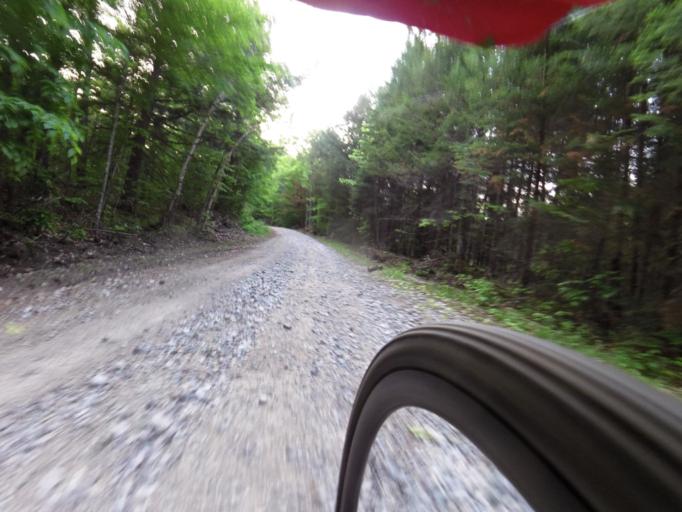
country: CA
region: Ontario
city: Arnprior
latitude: 45.1837
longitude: -76.5058
